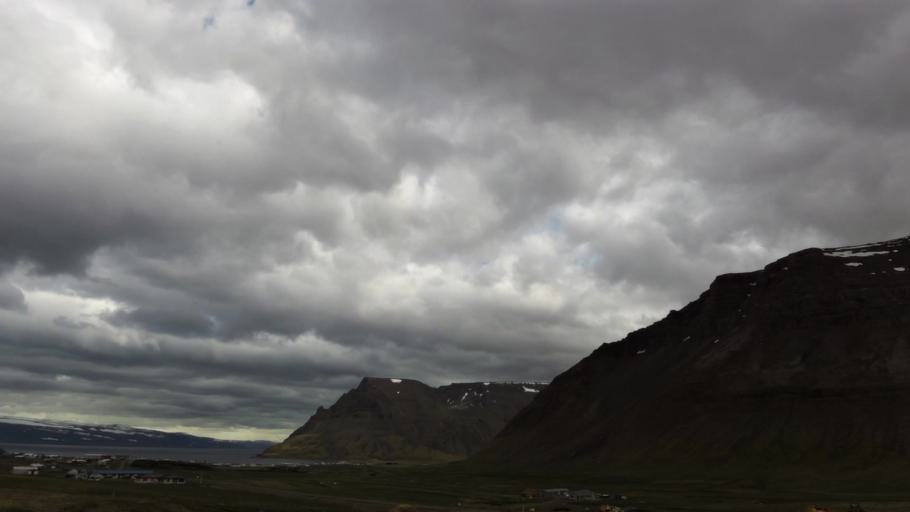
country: IS
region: Westfjords
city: Isafjoerdur
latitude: 66.1586
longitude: -23.2948
